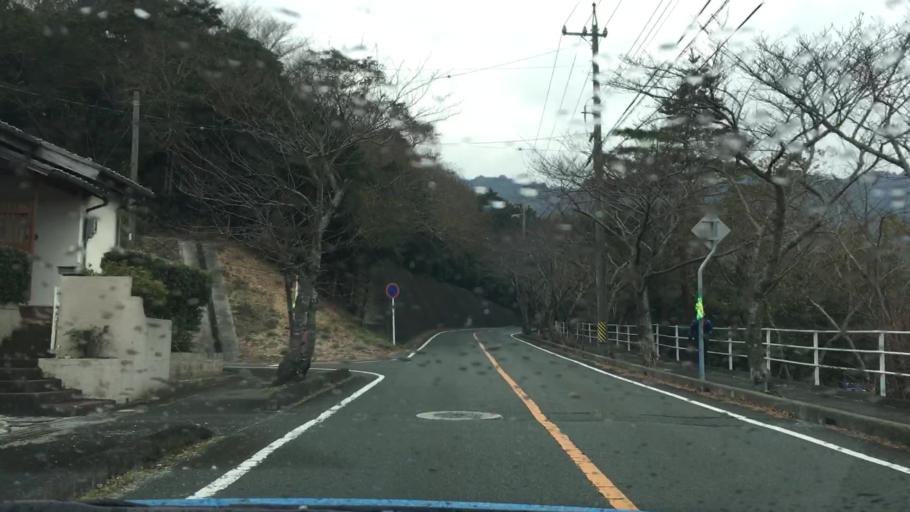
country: JP
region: Aichi
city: Tahara
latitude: 34.6690
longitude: 137.2478
